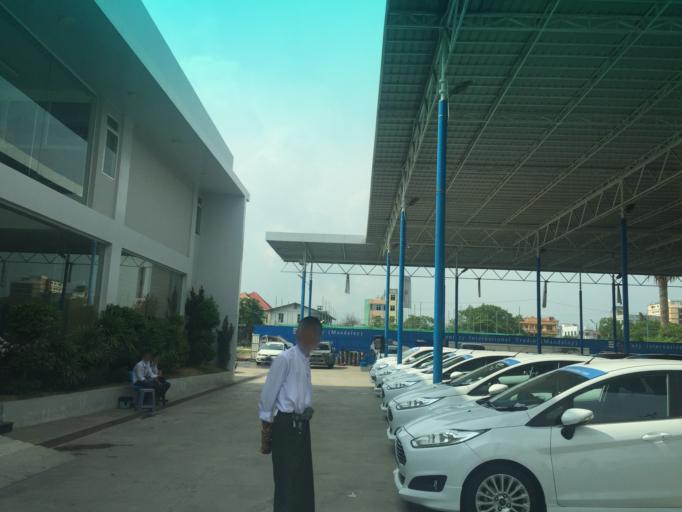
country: MM
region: Mandalay
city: Mandalay
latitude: 21.9684
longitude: 96.1000
